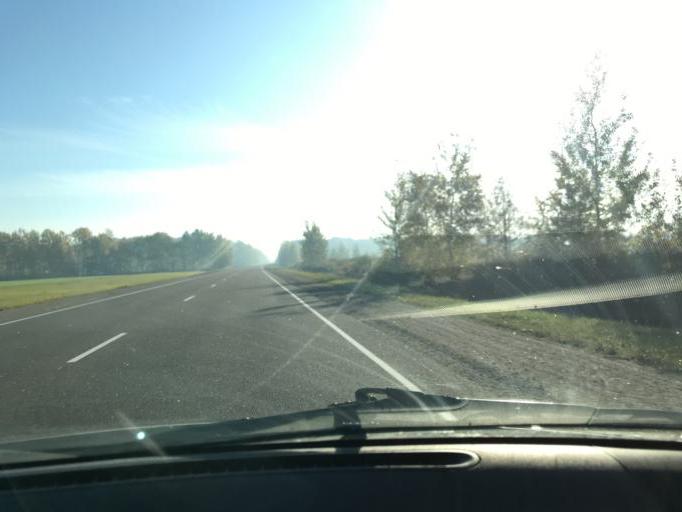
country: BY
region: Brest
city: Horad Luninyets
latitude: 52.3115
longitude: 26.6647
